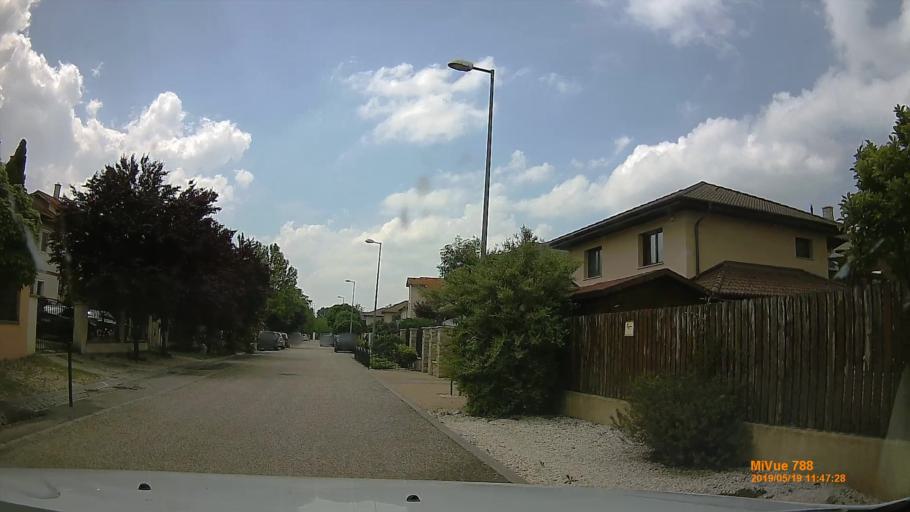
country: HU
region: Budapest
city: Budapest XVII. keruelet
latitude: 47.4704
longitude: 19.2229
